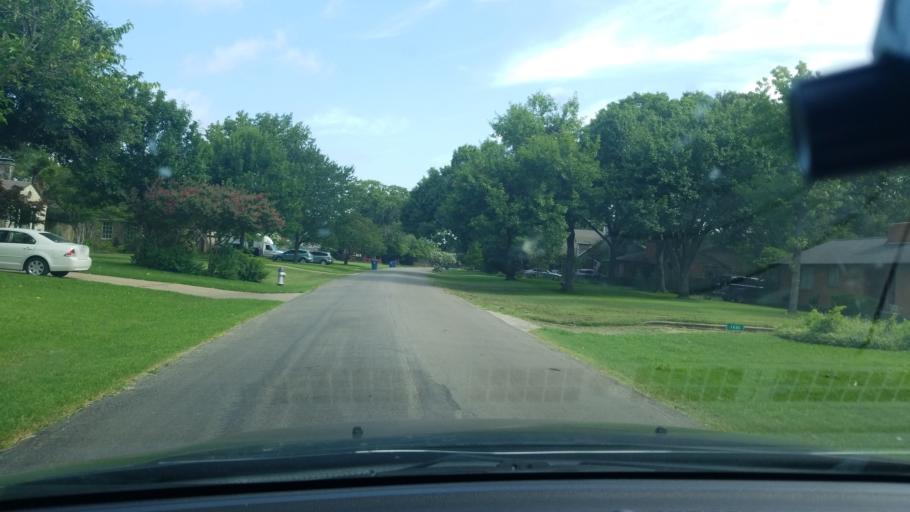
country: US
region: Texas
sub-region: Dallas County
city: Highland Park
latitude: 32.8272
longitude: -96.7004
